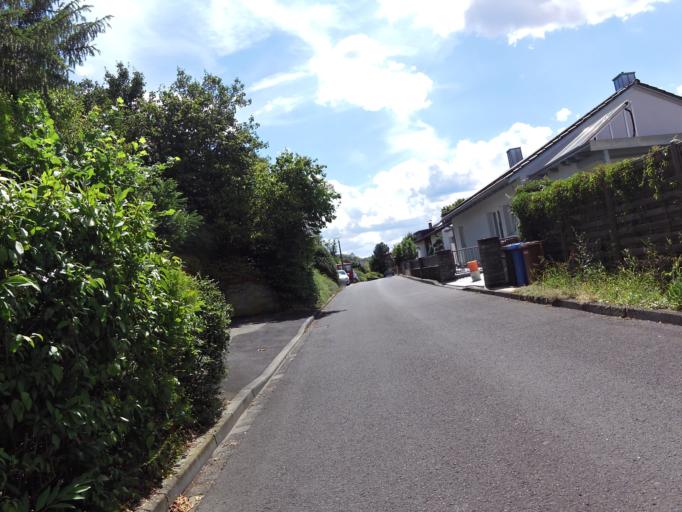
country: DE
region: Bavaria
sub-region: Regierungsbezirk Unterfranken
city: Wuerzburg
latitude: 49.8047
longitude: 9.9812
